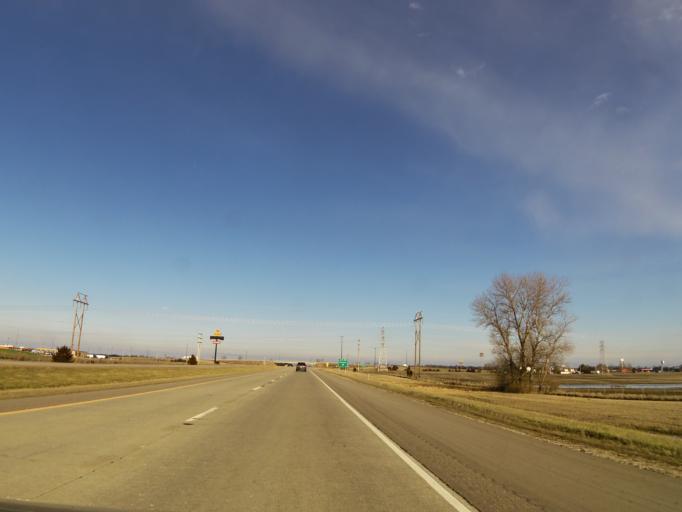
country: US
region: Illinois
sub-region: LaSalle County
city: Oglesby
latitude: 41.2886
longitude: -89.0823
